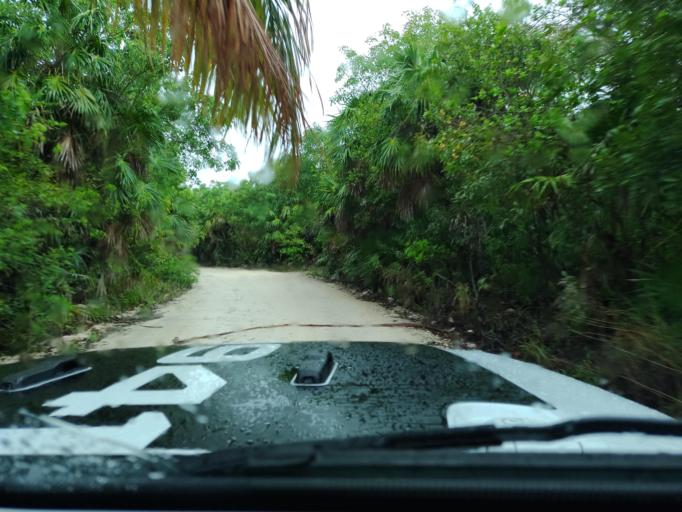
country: MX
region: Quintana Roo
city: Tulum
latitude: 19.9759
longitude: -87.4690
